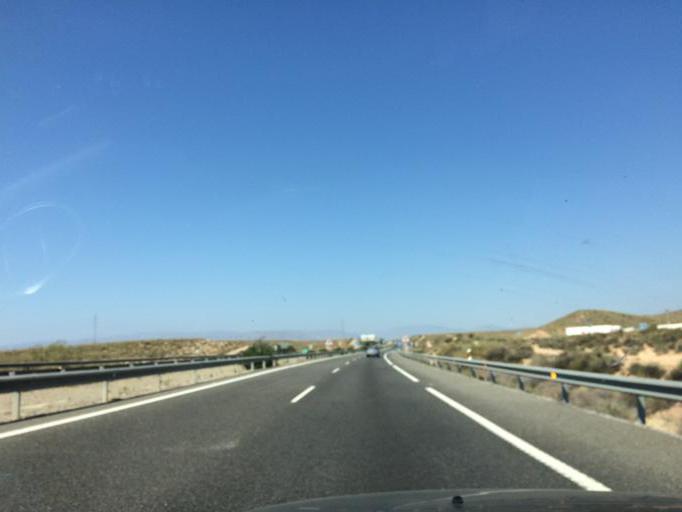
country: ES
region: Andalusia
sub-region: Provincia de Almeria
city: Retamar
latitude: 36.8739
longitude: -2.3373
